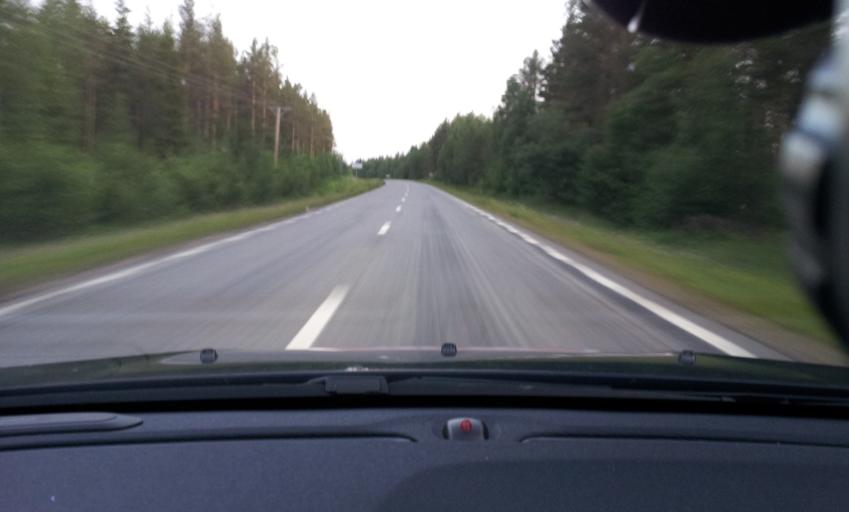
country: SE
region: Jaemtland
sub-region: Ragunda Kommun
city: Hammarstrand
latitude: 63.0135
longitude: 16.1237
